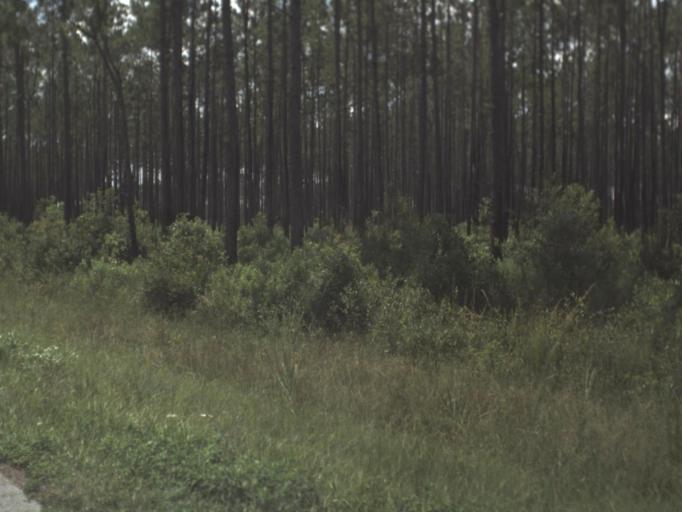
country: US
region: Florida
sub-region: Baker County
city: Macclenny
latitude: 30.5663
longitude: -82.4036
